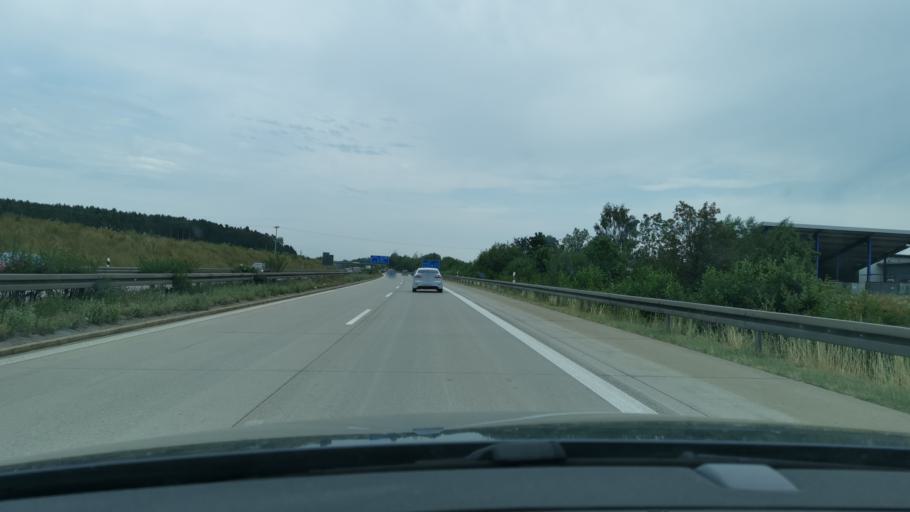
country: DE
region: Bavaria
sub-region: Upper Palatinate
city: Wernberg-Koblitz
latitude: 49.5315
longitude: 12.1416
